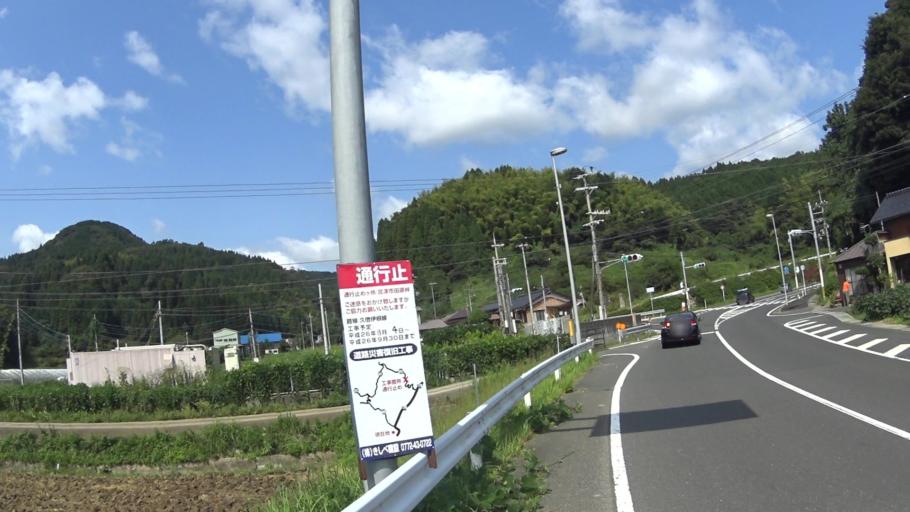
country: JP
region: Kyoto
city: Miyazu
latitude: 35.6581
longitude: 135.2573
